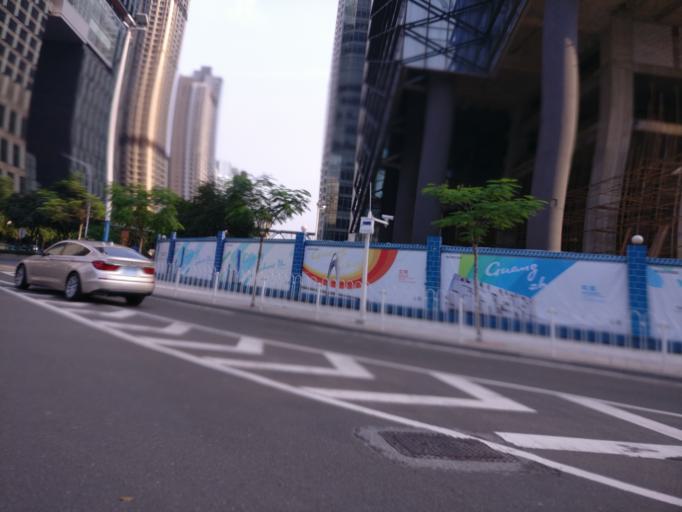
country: CN
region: Guangdong
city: Wushan
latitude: 23.1258
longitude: 113.3223
